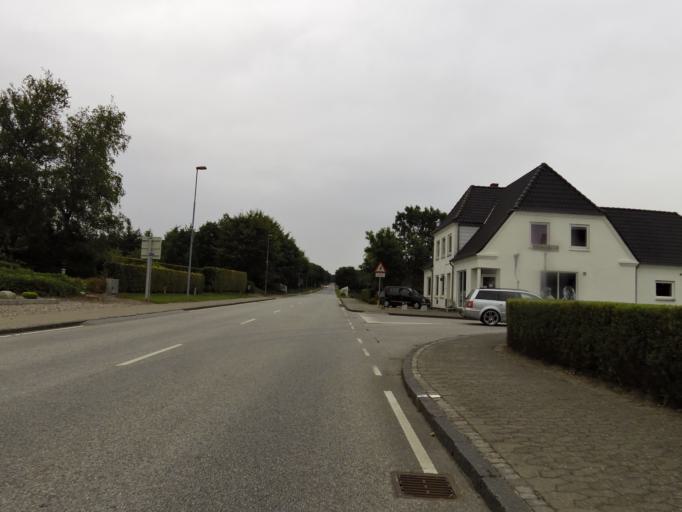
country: DK
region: South Denmark
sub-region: Tonder Kommune
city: Logumkloster
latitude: 55.1516
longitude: 8.9609
